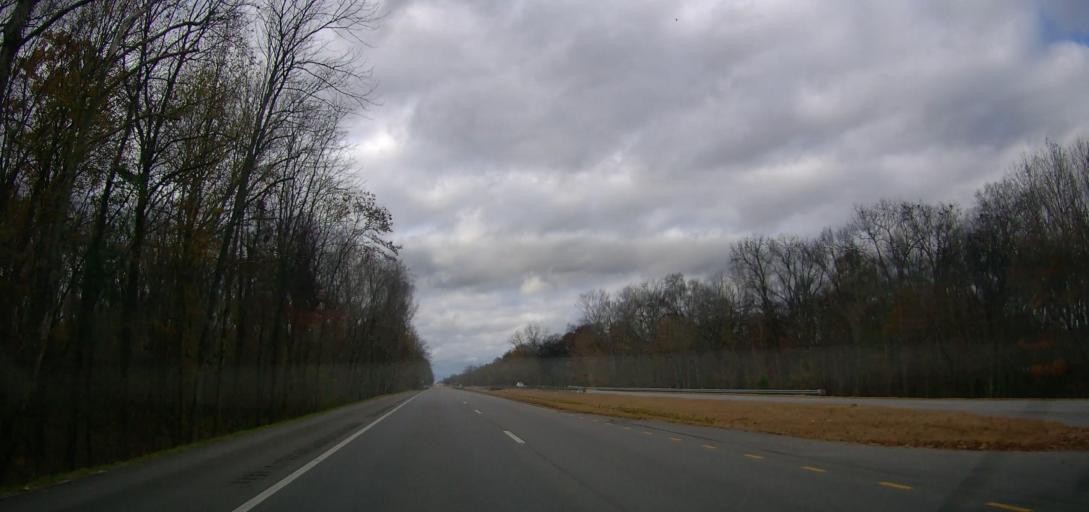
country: US
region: Alabama
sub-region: Lawrence County
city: Town Creek
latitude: 34.6307
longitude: -87.4847
